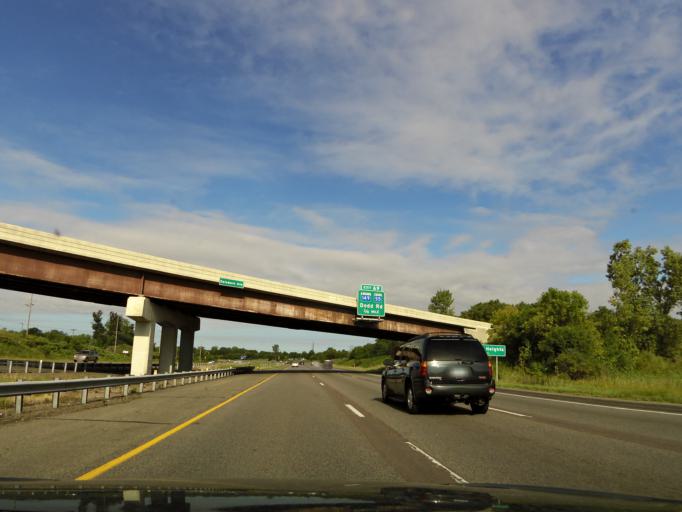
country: US
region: Minnesota
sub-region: Dakota County
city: Mendota Heights
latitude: 44.8609
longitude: -93.1051
